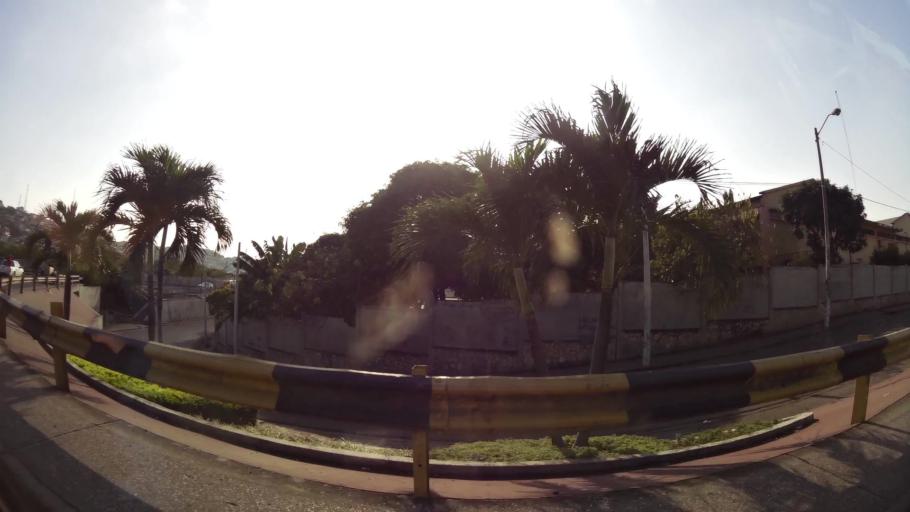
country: EC
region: Guayas
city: Guayaquil
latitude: -2.1488
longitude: -79.9123
